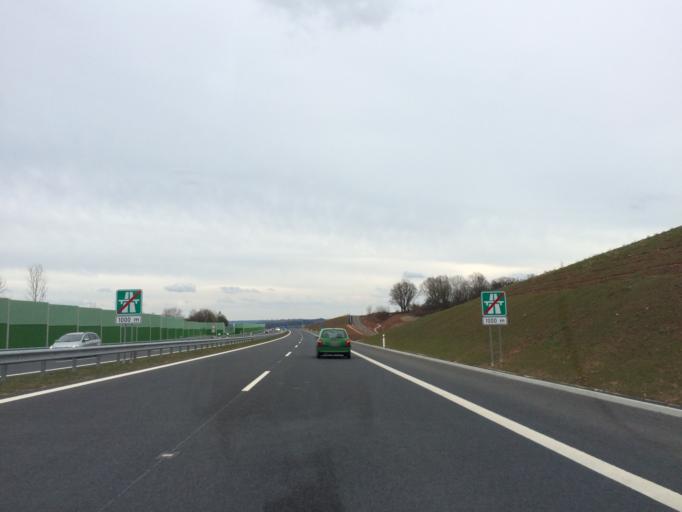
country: CZ
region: Ustecky
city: Lubenec
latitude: 50.1332
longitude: 13.2645
